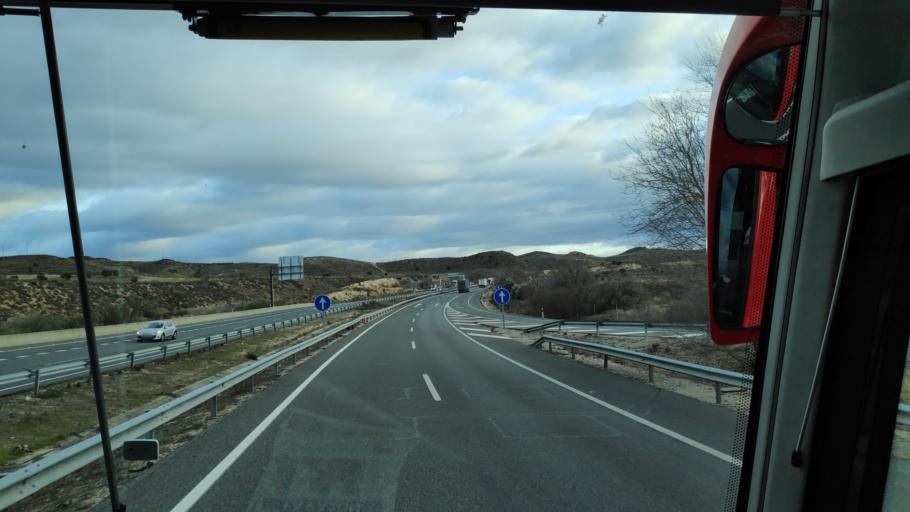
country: ES
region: Madrid
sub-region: Provincia de Madrid
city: Perales de Tajuna
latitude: 40.2226
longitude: -3.3312
